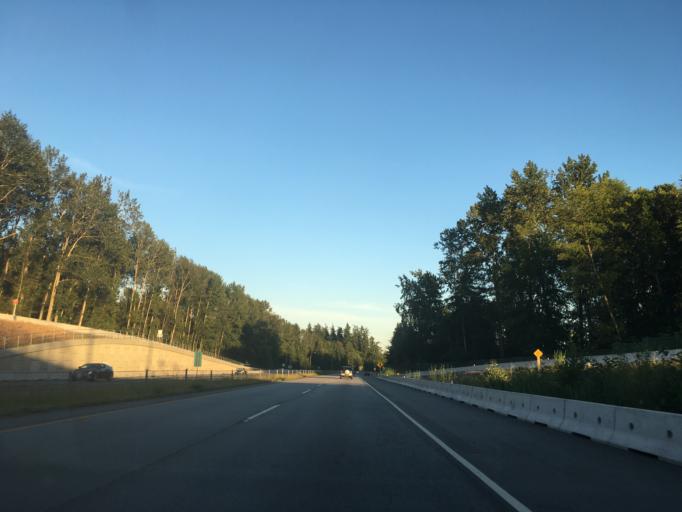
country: CA
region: British Columbia
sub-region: Greater Vancouver Regional District
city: White Rock
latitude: 49.0309
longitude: -122.7693
